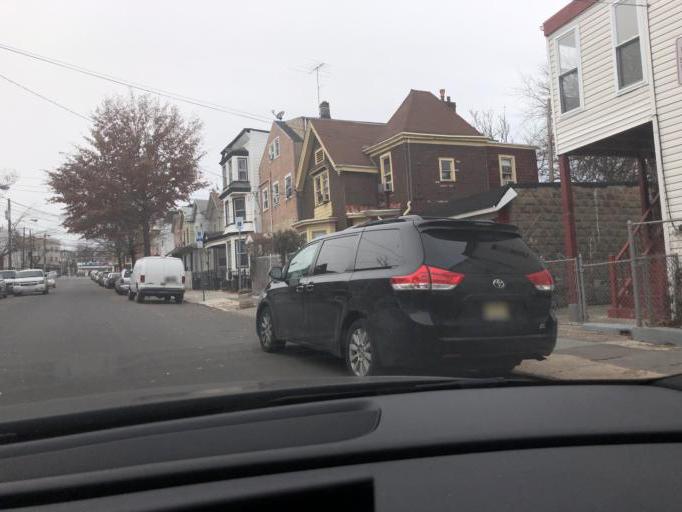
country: US
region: New Jersey
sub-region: Hudson County
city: East Newark
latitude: 40.7574
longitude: -74.1728
